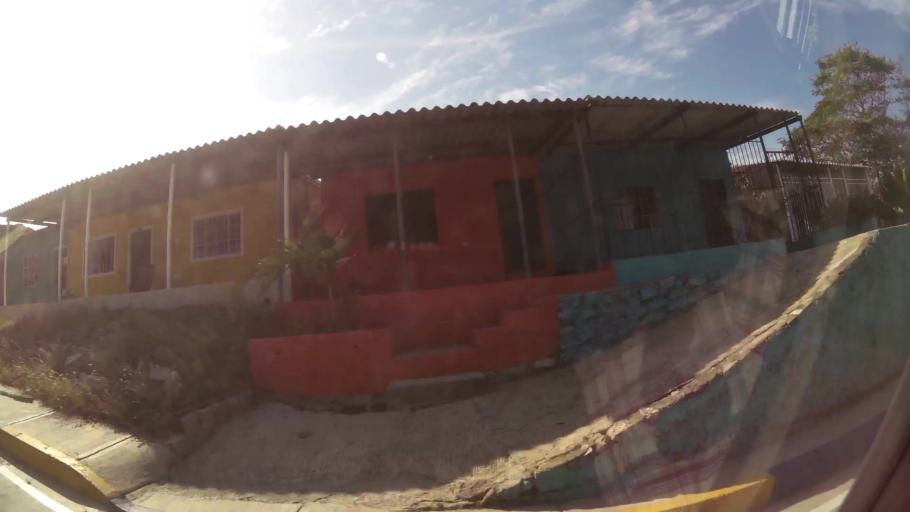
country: CO
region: Atlantico
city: Soledad
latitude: 10.9263
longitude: -74.8178
